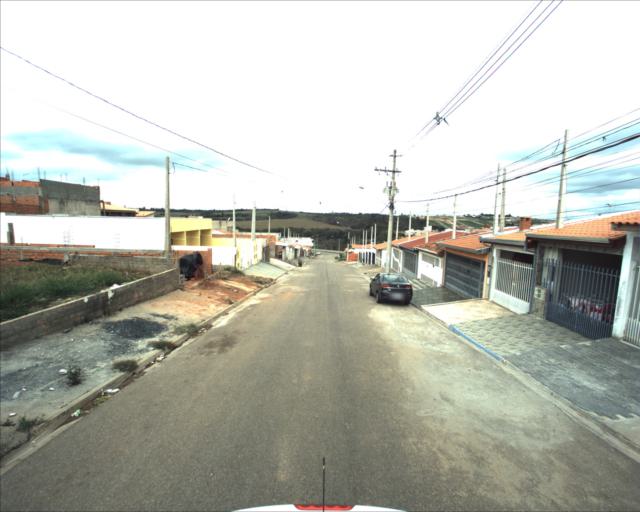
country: BR
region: Sao Paulo
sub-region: Sorocaba
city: Sorocaba
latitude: -23.4332
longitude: -47.5018
